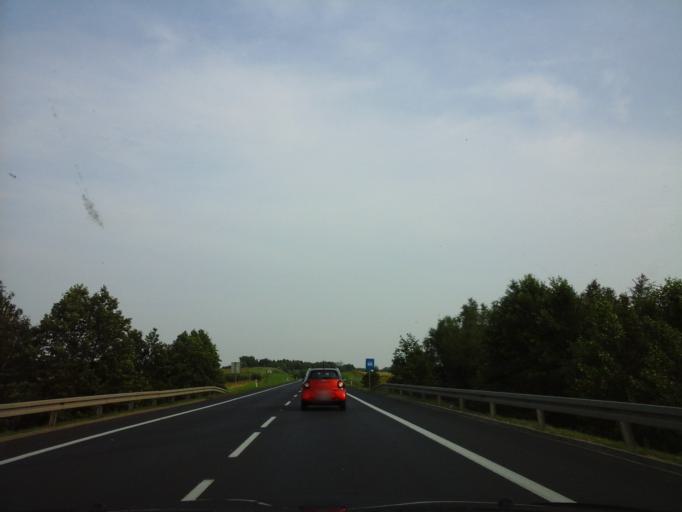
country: PL
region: Greater Poland Voivodeship
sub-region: Powiat koscianski
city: Smigiel
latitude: 52.0211
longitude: 16.5384
